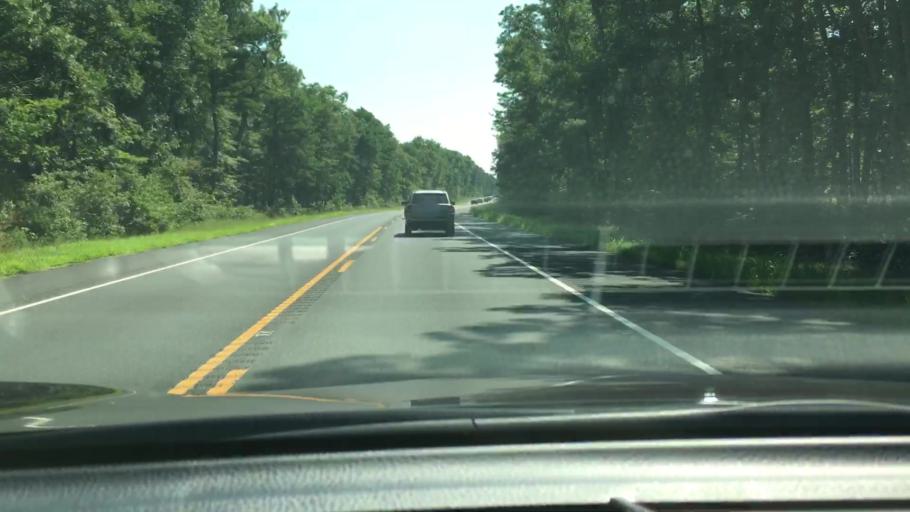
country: US
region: New Jersey
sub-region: Cape May County
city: Woodbine
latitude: 39.3176
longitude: -74.8437
